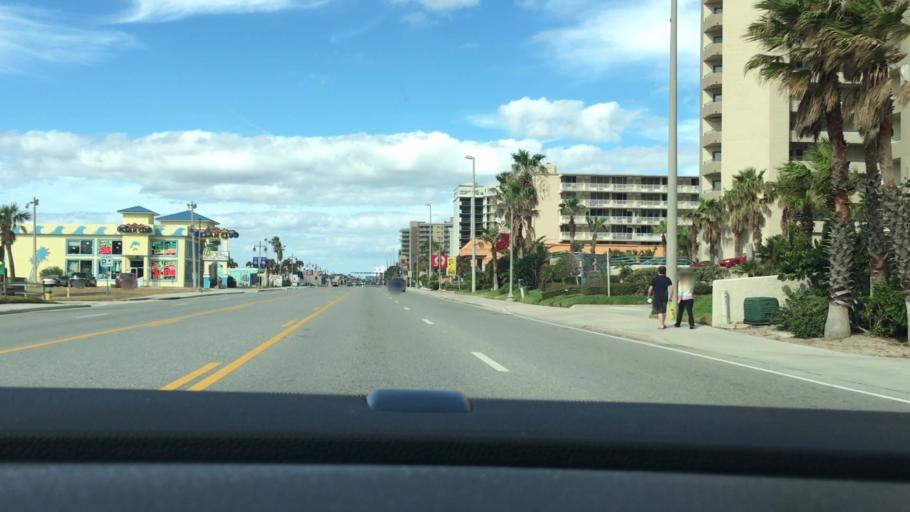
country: US
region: Florida
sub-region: Volusia County
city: Daytona Beach Shores
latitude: 29.1988
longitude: -80.9944
